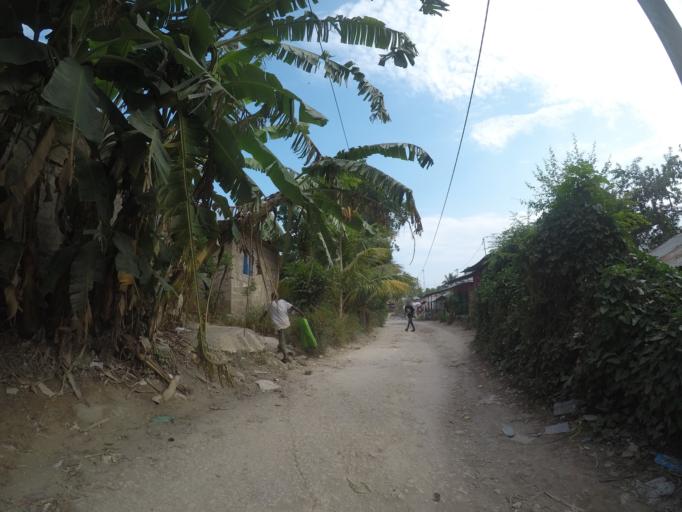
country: TZ
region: Zanzibar Urban/West
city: Zanzibar
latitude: -6.1762
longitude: 39.2072
